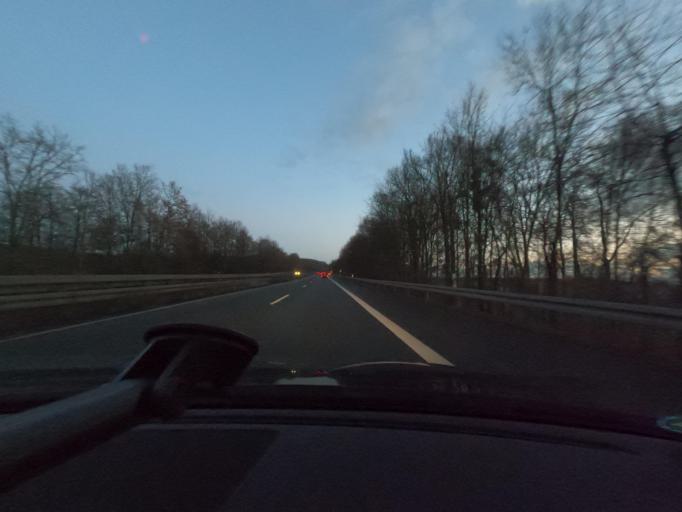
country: DE
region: Lower Saxony
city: Herzberg am Harz
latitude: 51.6435
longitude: 10.3546
